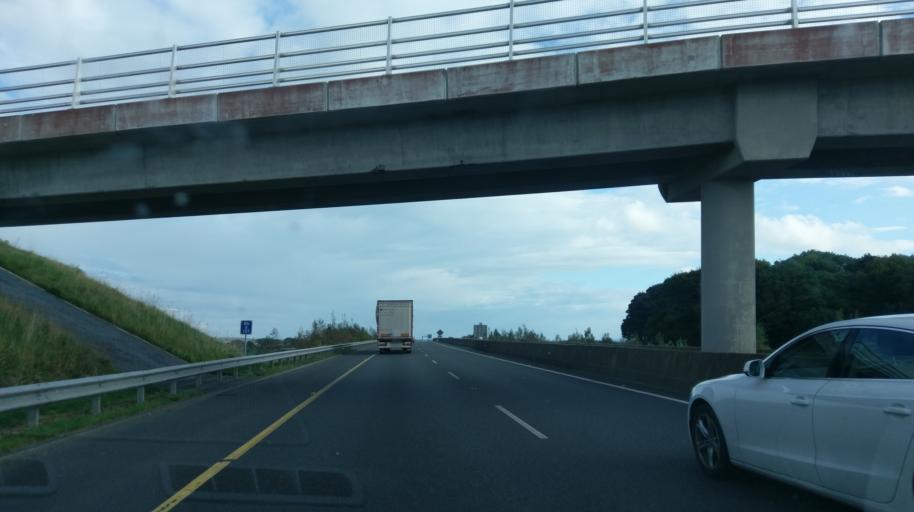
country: IE
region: Connaught
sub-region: County Galway
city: Athenry
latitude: 53.2935
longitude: -8.7771
